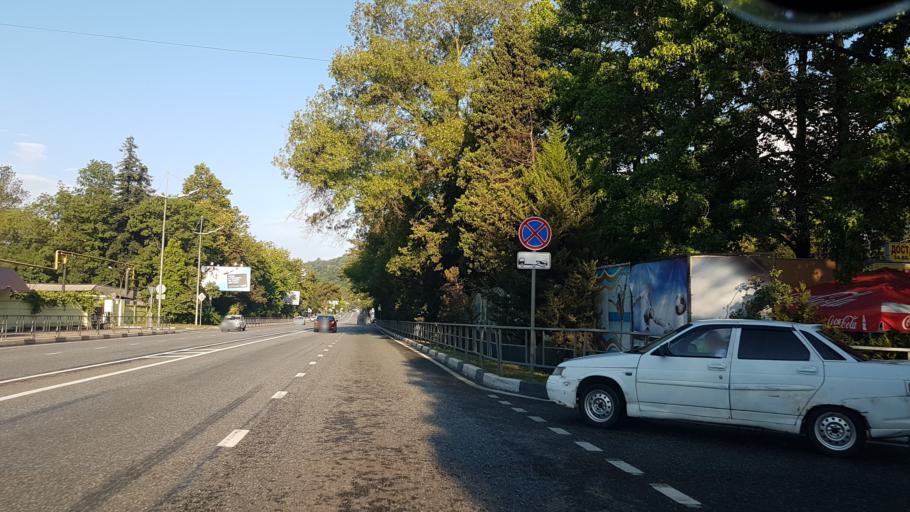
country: RU
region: Krasnodarskiy
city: Dagomys
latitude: 43.6613
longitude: 39.6646
